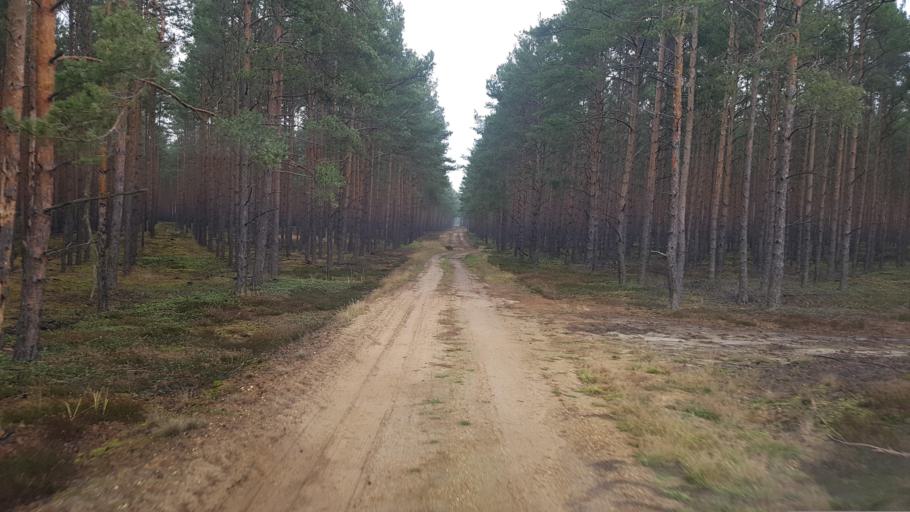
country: DE
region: Brandenburg
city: Sallgast
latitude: 51.6451
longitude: 13.8148
